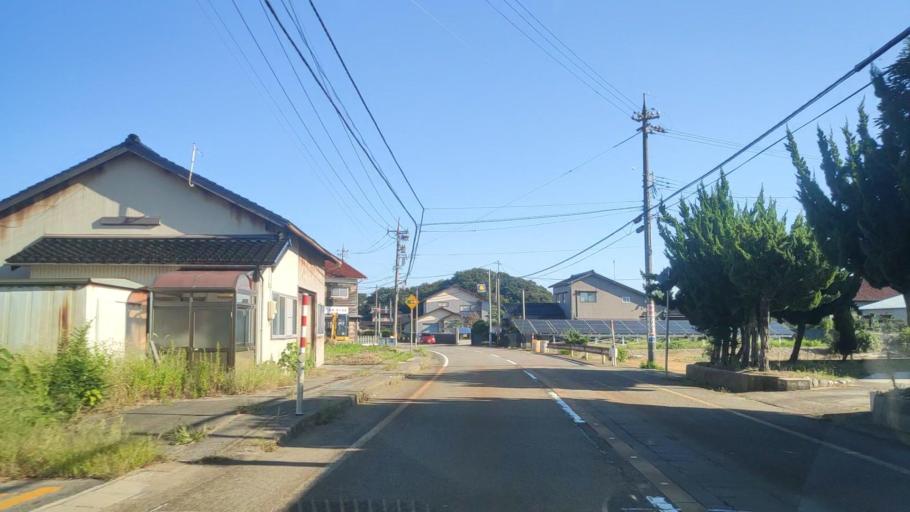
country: JP
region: Ishikawa
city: Hakui
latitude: 36.8275
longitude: 136.7585
